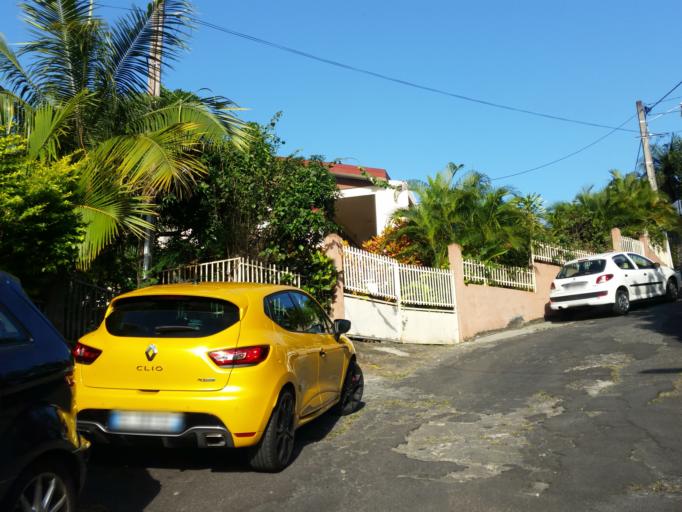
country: RE
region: Reunion
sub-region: Reunion
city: Saint-Denis
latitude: -20.8989
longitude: 55.4577
